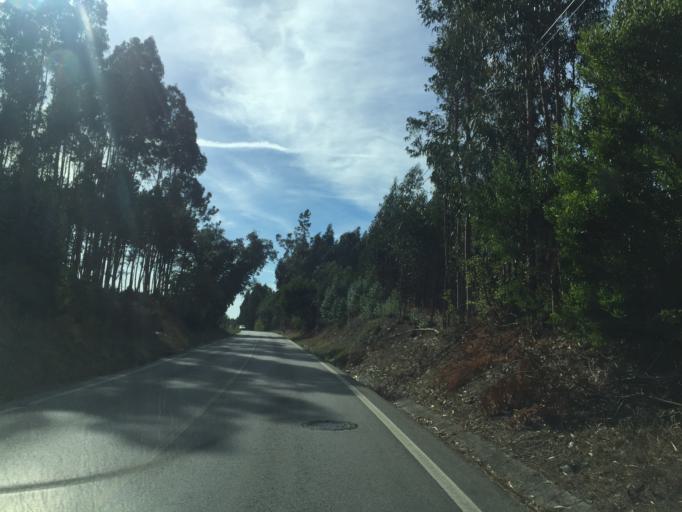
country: PT
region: Coimbra
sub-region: Figueira da Foz
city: Lavos
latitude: 40.0813
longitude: -8.8236
